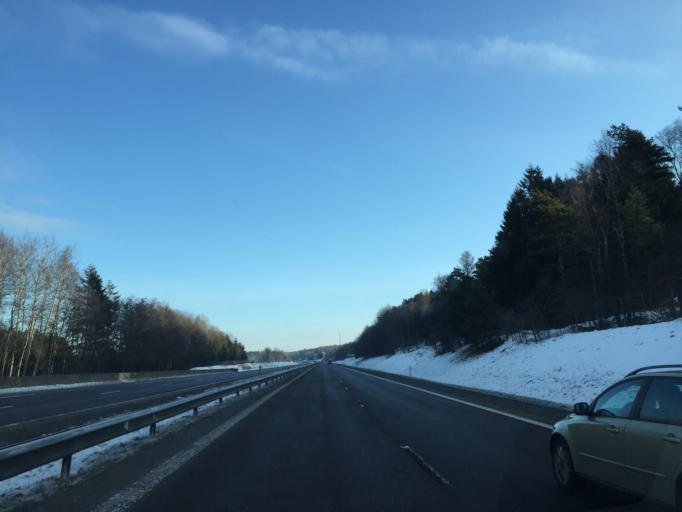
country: SE
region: Vaestra Goetaland
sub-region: Stenungsunds Kommun
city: Stora Hoga
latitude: 58.0465
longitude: 11.8549
